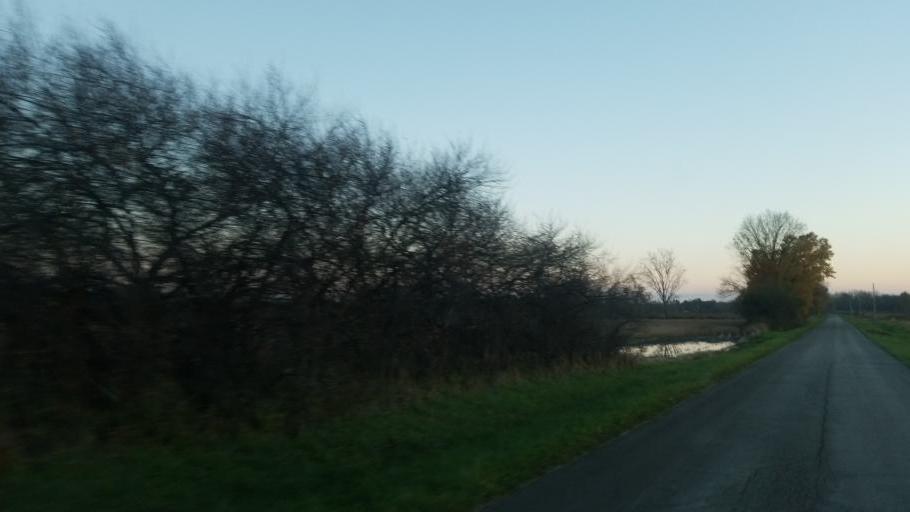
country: US
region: Ohio
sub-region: Huron County
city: Willard
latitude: 41.0322
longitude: -82.7820
